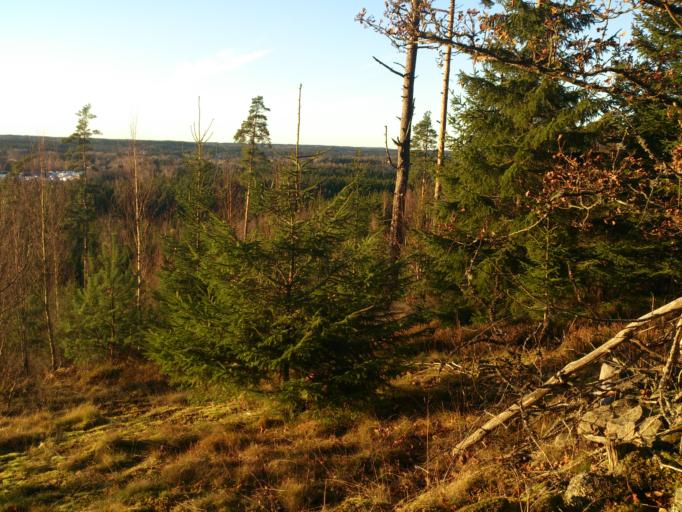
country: SE
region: Kronoberg
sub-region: Alvesta Kommun
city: Moheda
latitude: 57.0085
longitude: 14.5902
